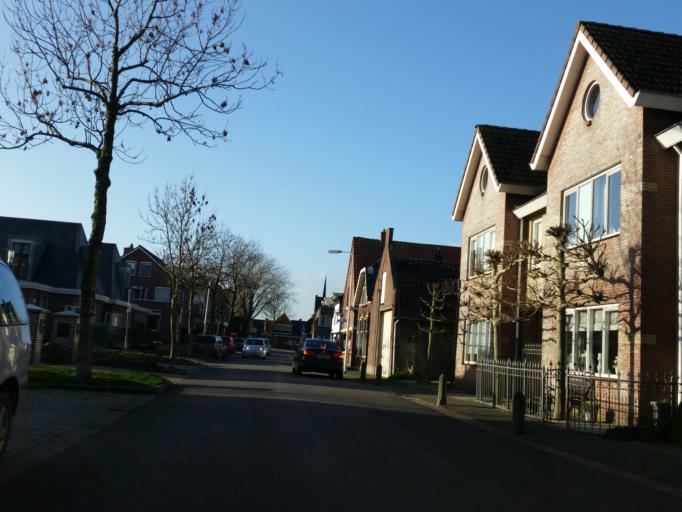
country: NL
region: South Holland
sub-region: Gemeente Rijnwoude
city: Benthuizen
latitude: 52.0439
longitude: 4.5774
